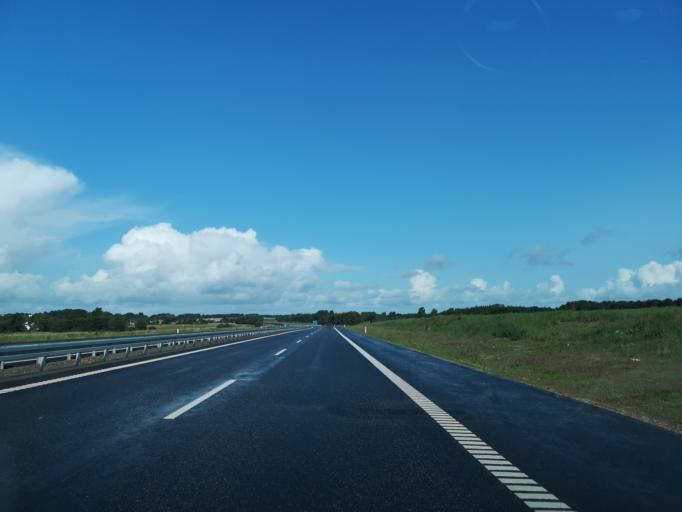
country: DK
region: Central Jutland
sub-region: Herning Kommune
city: Snejbjerg
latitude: 56.2110
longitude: 8.8644
